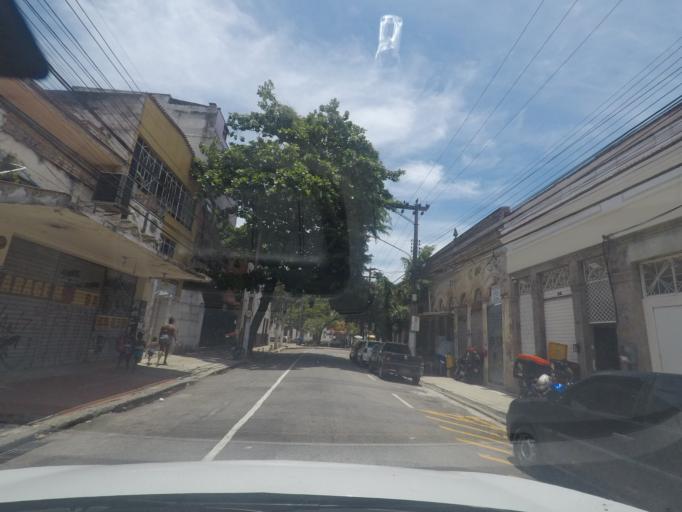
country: BR
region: Rio de Janeiro
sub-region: Niteroi
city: Niteroi
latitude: -22.8998
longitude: -43.1297
